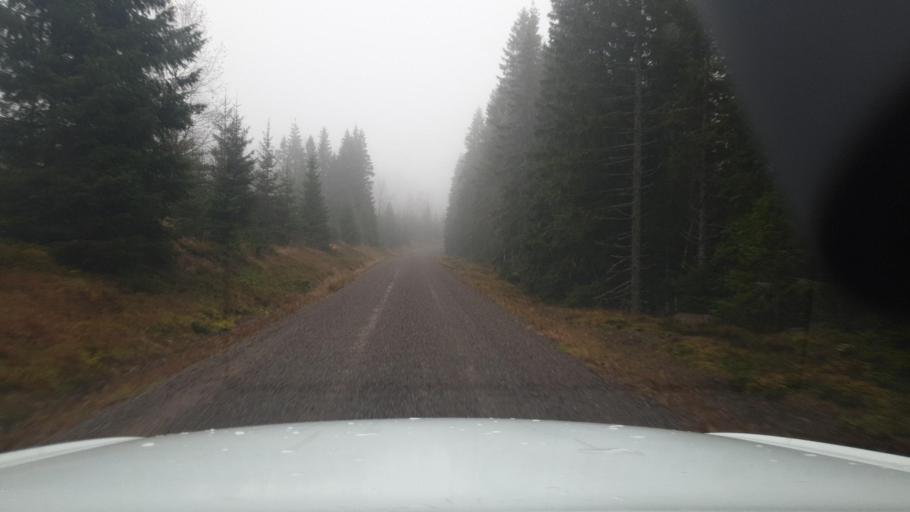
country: SE
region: Vaermland
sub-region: Eda Kommun
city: Charlottenberg
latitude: 60.0919
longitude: 12.6151
